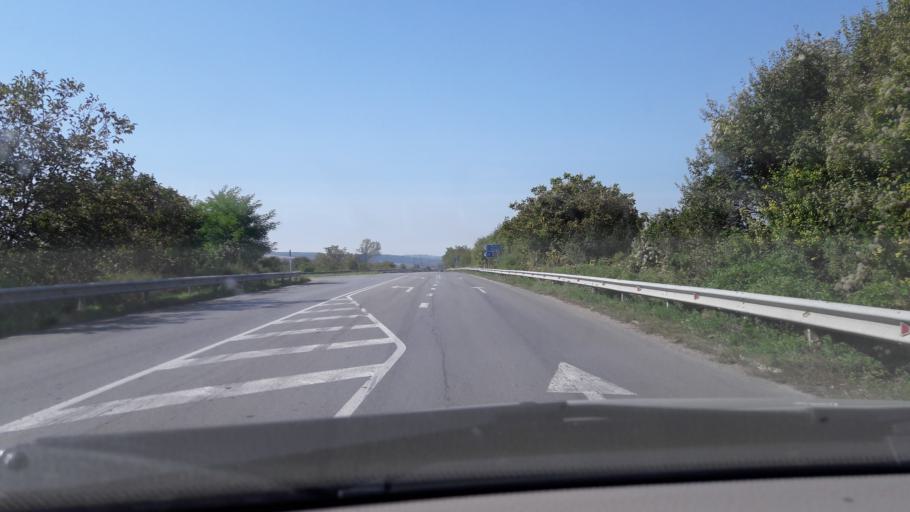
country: BG
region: Razgrad
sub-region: Obshtina Razgrad
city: Razgrad
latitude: 43.5472
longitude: 26.4855
